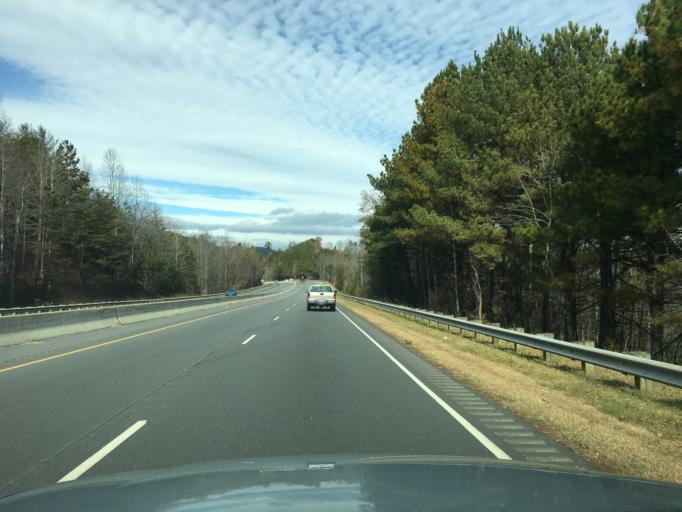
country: US
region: North Carolina
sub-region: McDowell County
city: Marion
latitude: 35.6923
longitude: -82.0301
